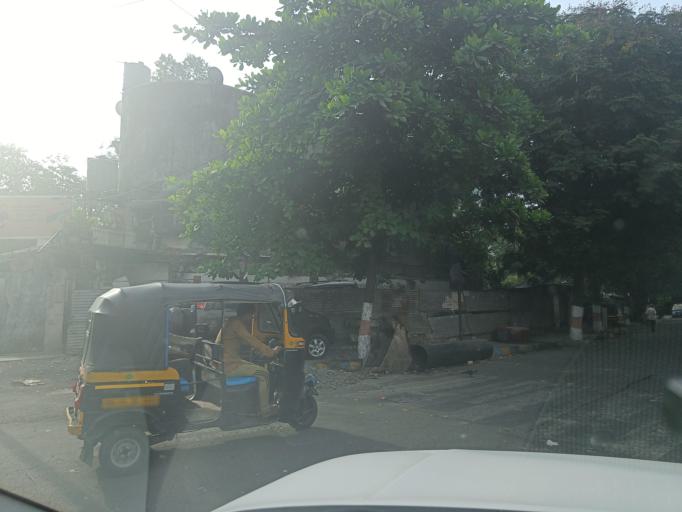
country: IN
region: Maharashtra
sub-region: Thane
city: Thane
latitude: 19.1882
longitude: 72.9640
